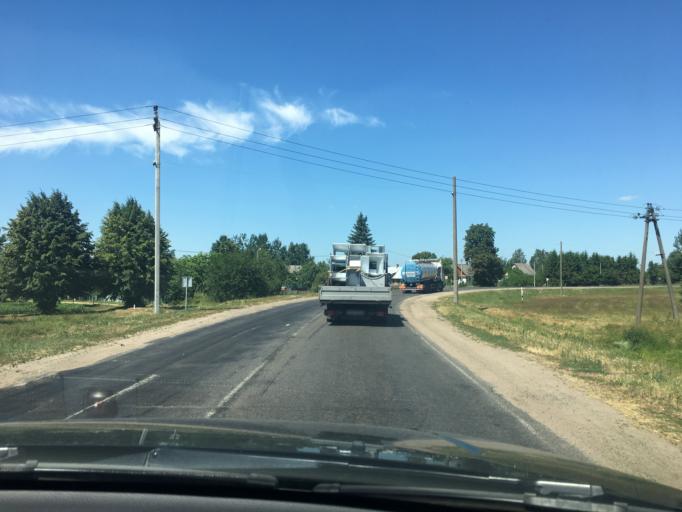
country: BY
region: Grodnenskaya
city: Iwye
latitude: 54.0611
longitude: 25.9111
